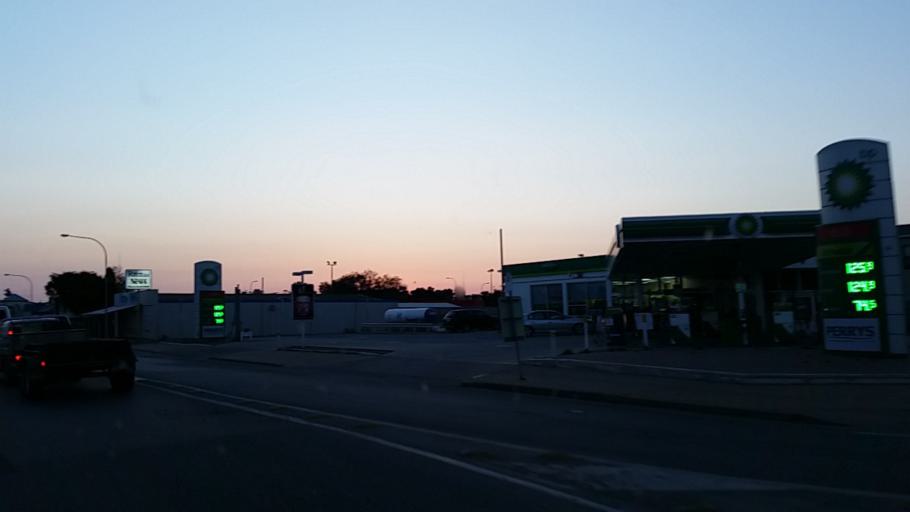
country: AU
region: South Australia
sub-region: Port Pirie City and Dists
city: Port Pirie
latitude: -33.1803
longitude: 138.0119
